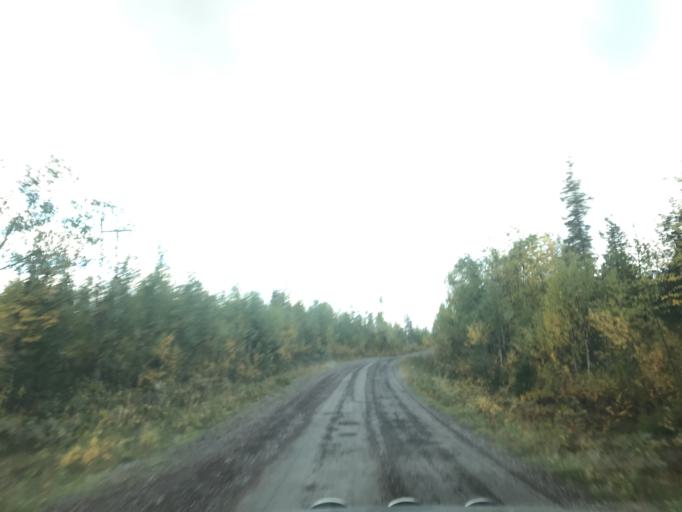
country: SE
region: Norrbotten
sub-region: Gallivare Kommun
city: Malmberget
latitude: 67.5871
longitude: 20.8732
